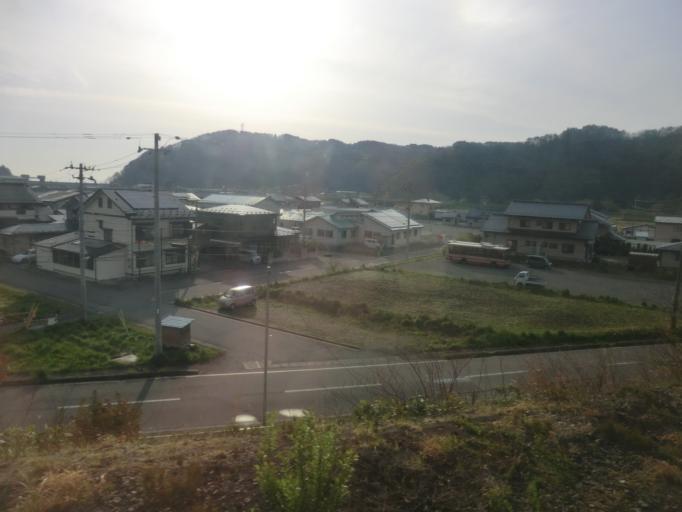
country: JP
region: Iwate
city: Miyako
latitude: 39.8439
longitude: 141.9582
